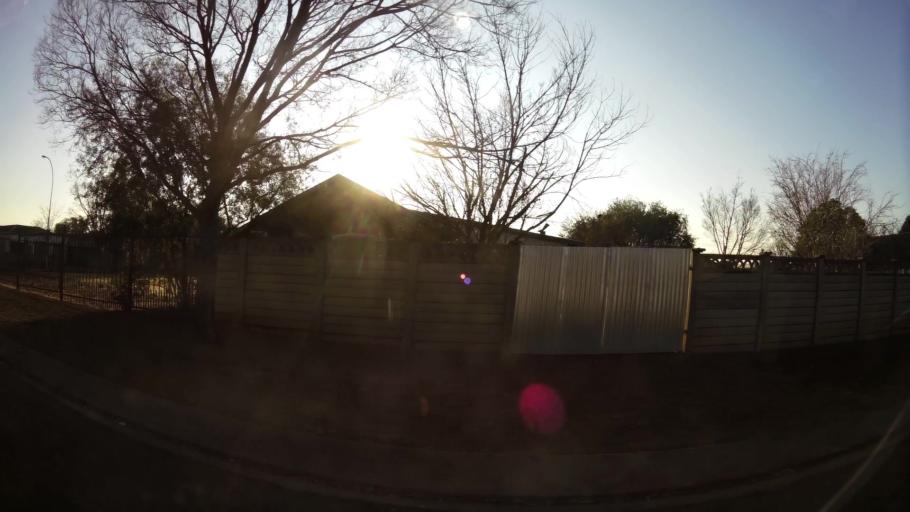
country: ZA
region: Orange Free State
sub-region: Mangaung Metropolitan Municipality
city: Bloemfontein
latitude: -29.1599
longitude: 26.1748
